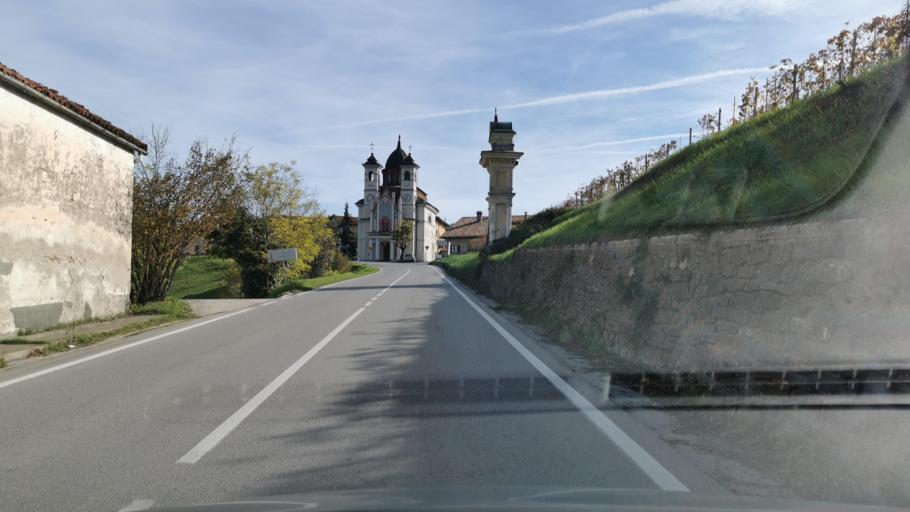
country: IT
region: Piedmont
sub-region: Provincia di Cuneo
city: Dogliani
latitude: 44.5197
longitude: 7.9527
